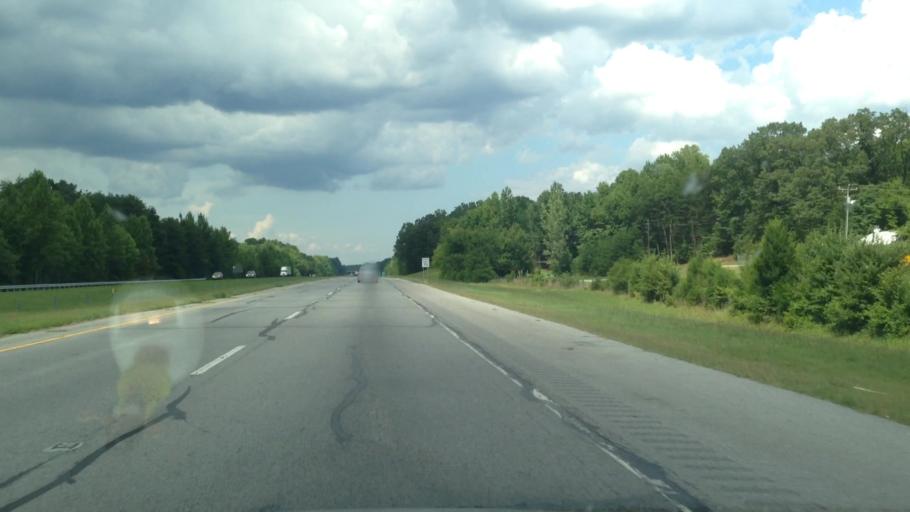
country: US
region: Virginia
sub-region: City of Danville
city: Danville
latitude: 36.4940
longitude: -79.4844
